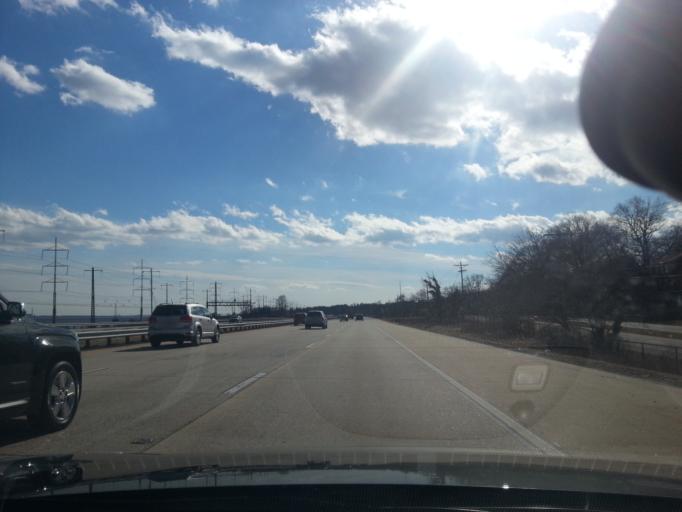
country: US
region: Delaware
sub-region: New Castle County
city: Claymont
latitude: 39.7838
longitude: -75.4729
